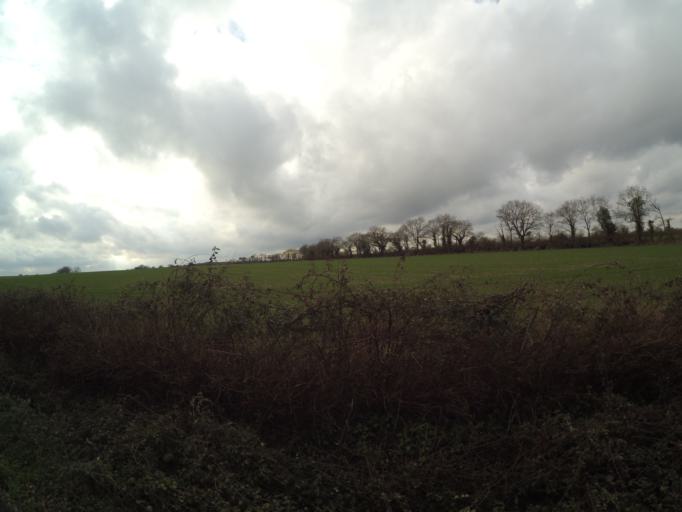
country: FR
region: Pays de la Loire
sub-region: Departement de la Vendee
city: La Bernardiere
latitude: 47.0260
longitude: -1.2924
